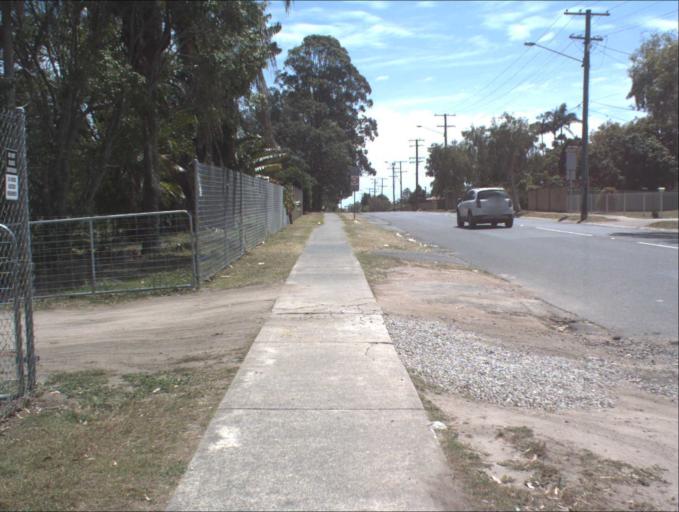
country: AU
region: Queensland
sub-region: Logan
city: Rochedale South
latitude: -27.5921
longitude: 153.1225
